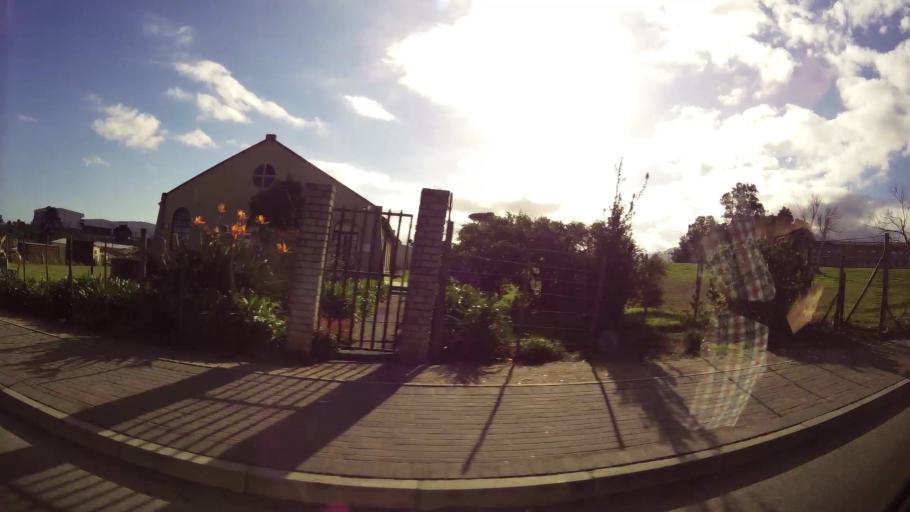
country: ZA
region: Western Cape
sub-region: Eden District Municipality
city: George
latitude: -33.9767
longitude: 22.4783
